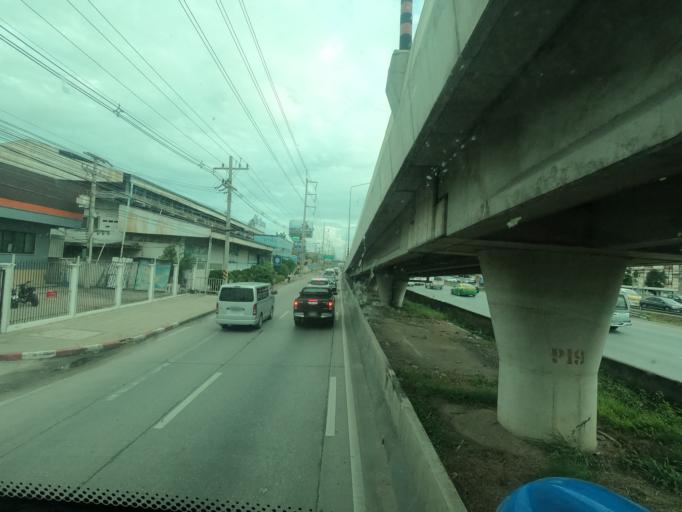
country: TH
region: Pathum Thani
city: Khlong Luang
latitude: 14.1201
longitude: 100.6188
